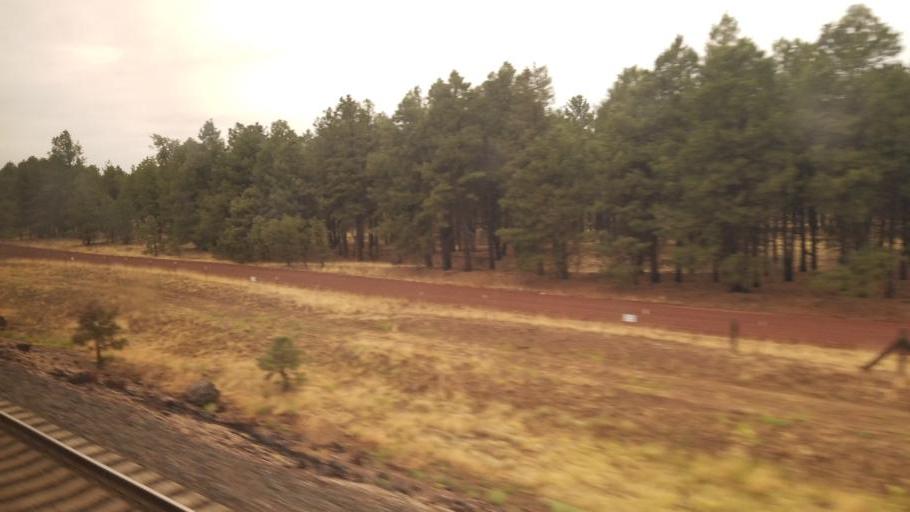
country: US
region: Arizona
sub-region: Coconino County
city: Flagstaff
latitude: 35.2180
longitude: -111.7914
